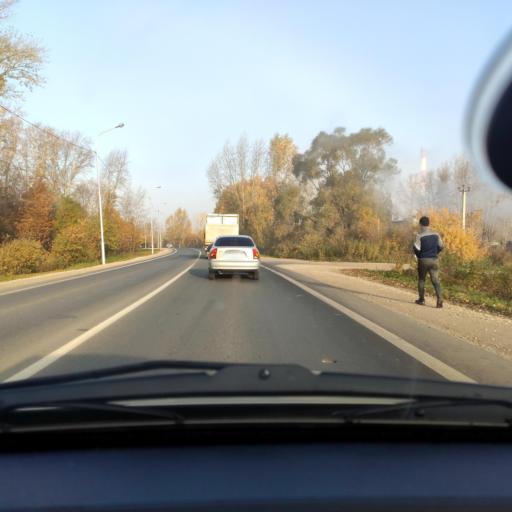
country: RU
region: Bashkortostan
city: Ufa
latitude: 54.8378
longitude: 56.1314
